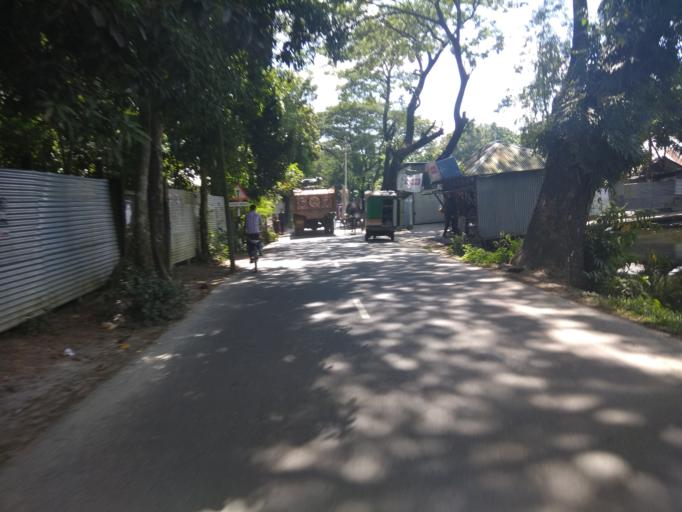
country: BD
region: Dhaka
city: Narayanganj
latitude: 23.4364
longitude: 90.4890
